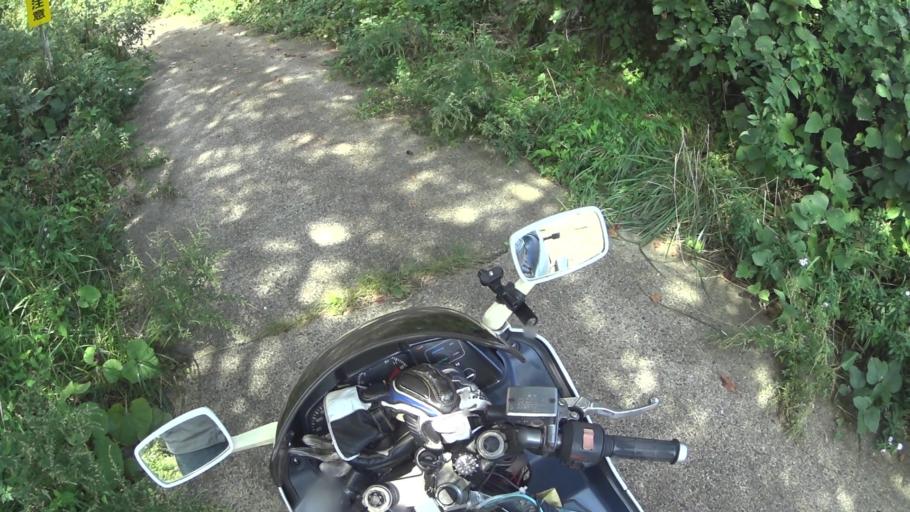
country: JP
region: Kyoto
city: Miyazu
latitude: 35.7200
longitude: 135.1864
